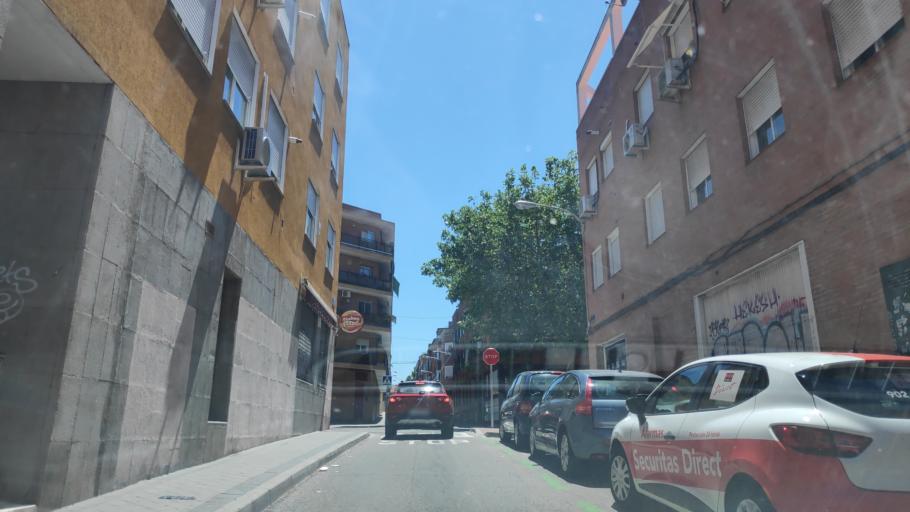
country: ES
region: Madrid
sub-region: Provincia de Madrid
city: Chamartin
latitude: 40.4673
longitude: -3.6943
